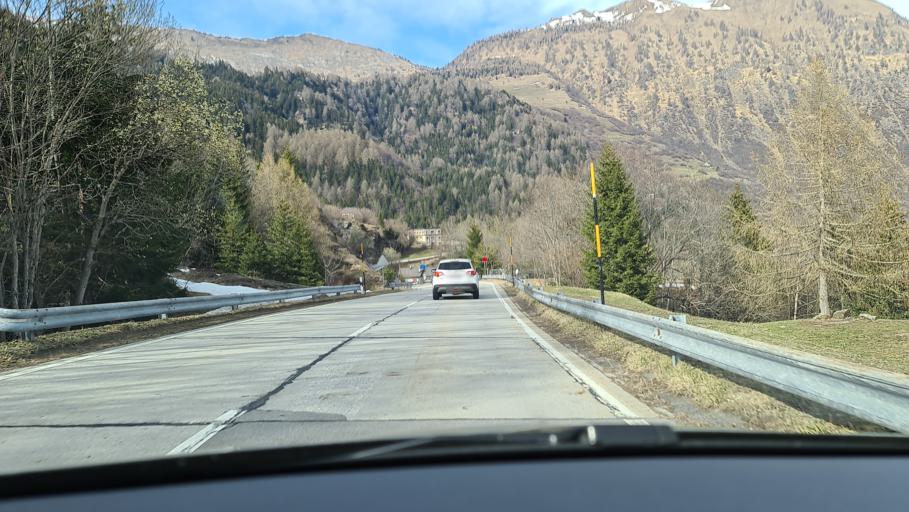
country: CH
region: Ticino
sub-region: Blenio District
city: Cancori
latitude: 46.5229
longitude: 8.9044
